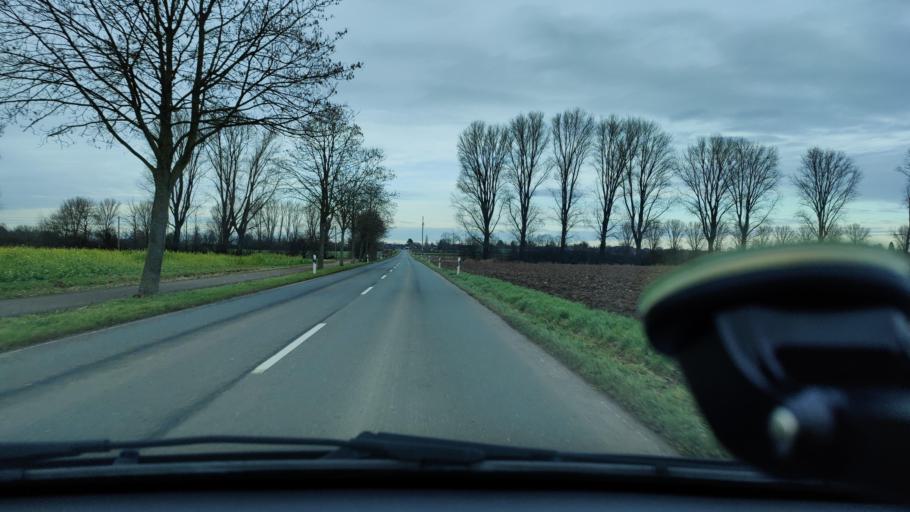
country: DE
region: North Rhine-Westphalia
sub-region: Regierungsbezirk Dusseldorf
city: Alpen
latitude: 51.6320
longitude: 6.5342
